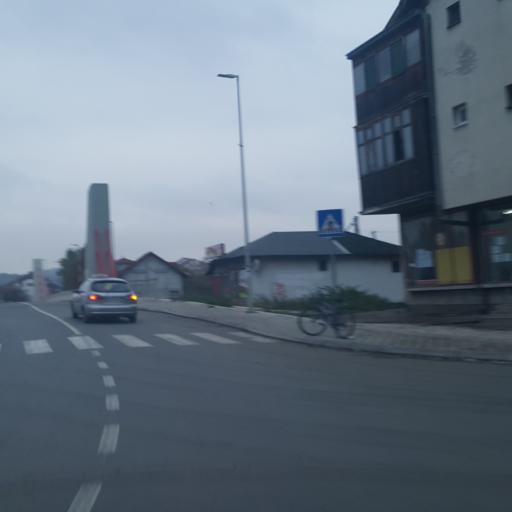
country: RS
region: Central Serbia
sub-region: Zajecarski Okrug
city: Zajecar
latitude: 43.9047
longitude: 22.2644
